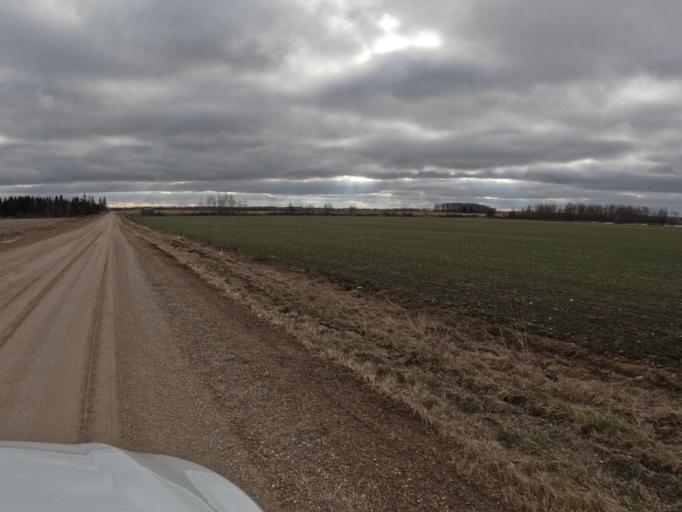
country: CA
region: Ontario
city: Shelburne
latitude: 43.8714
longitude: -80.4022
